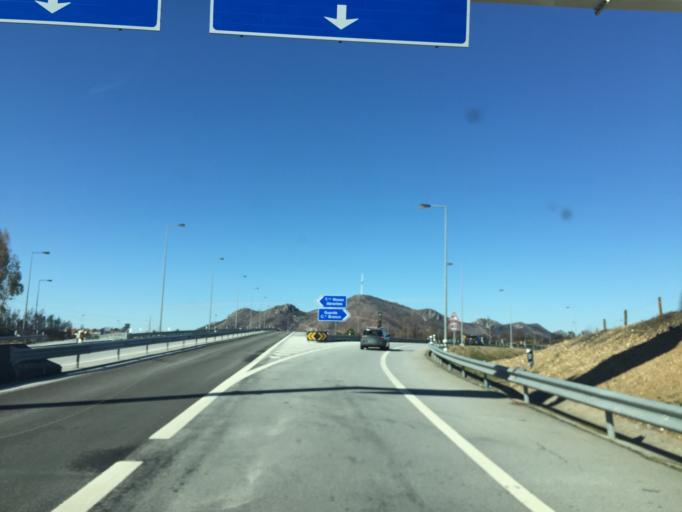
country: PT
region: Portalegre
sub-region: Nisa
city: Nisa
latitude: 39.5577
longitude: -7.7990
